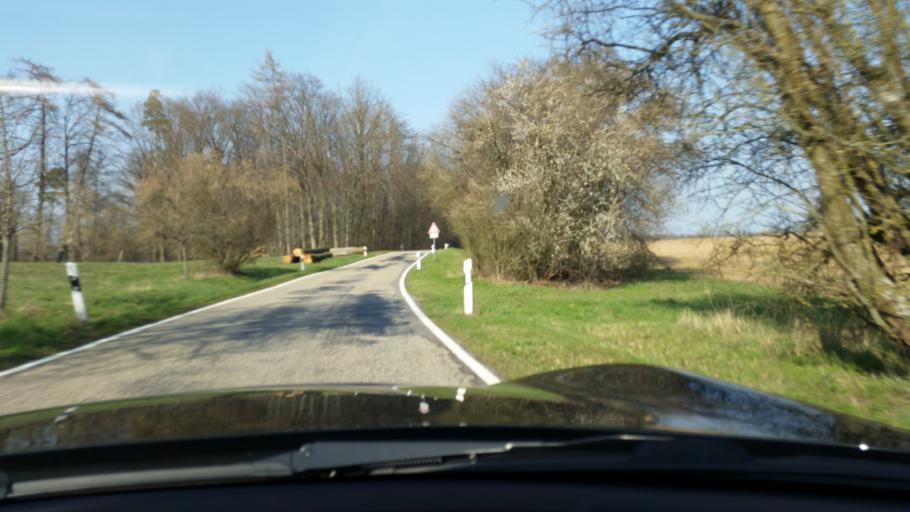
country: DE
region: Baden-Wuerttemberg
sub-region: Regierungsbezirk Stuttgart
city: Mockmuhl
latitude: 49.3412
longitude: 9.3719
